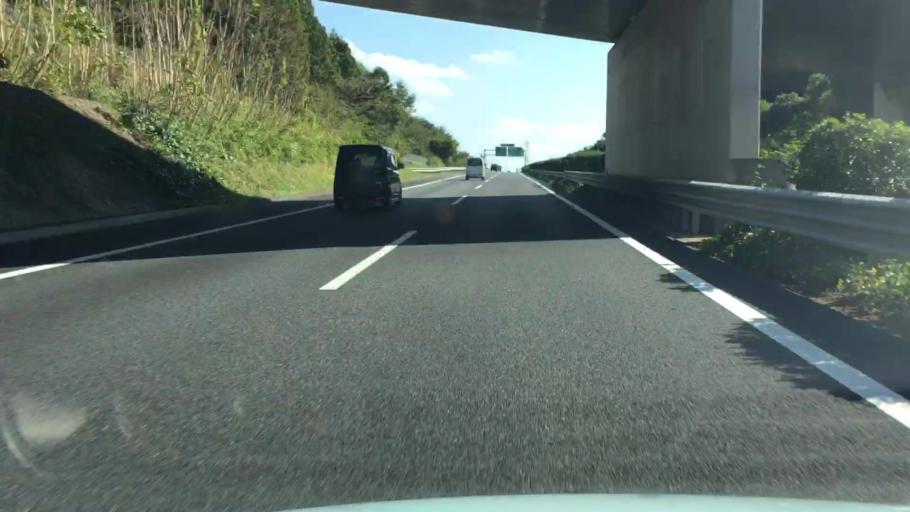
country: JP
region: Ibaraki
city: Tomobe
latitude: 36.3177
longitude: 140.3296
